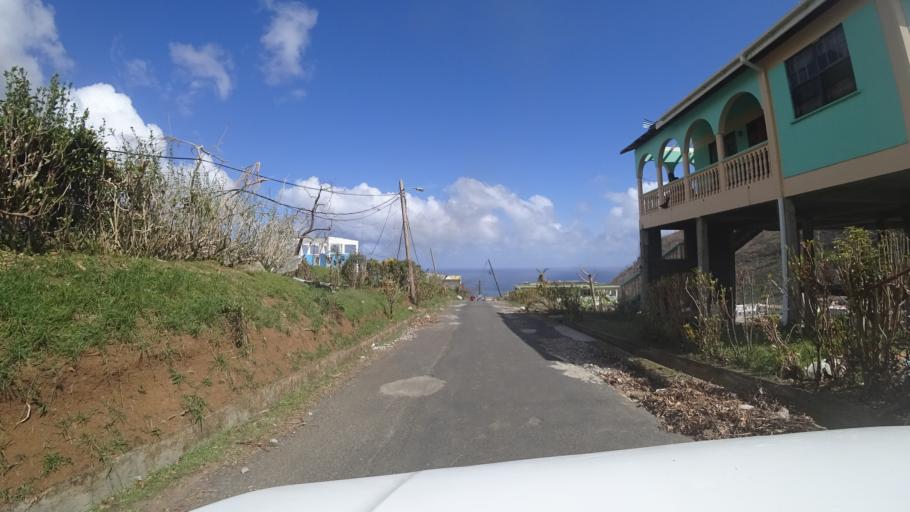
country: DM
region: Saint Patrick
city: Berekua
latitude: 15.2439
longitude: -61.3207
